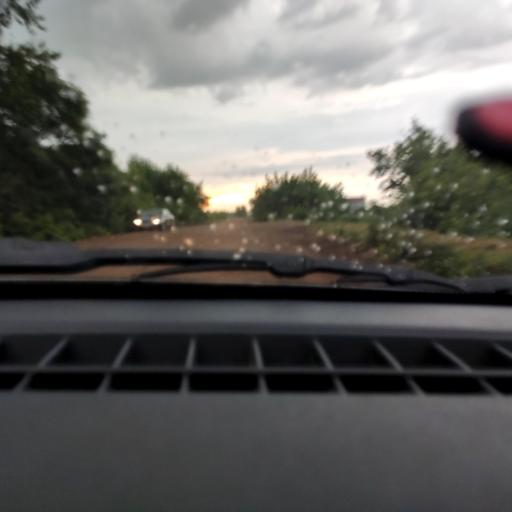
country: RU
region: Bashkortostan
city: Blagoveshchensk
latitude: 54.9264
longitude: 55.9694
